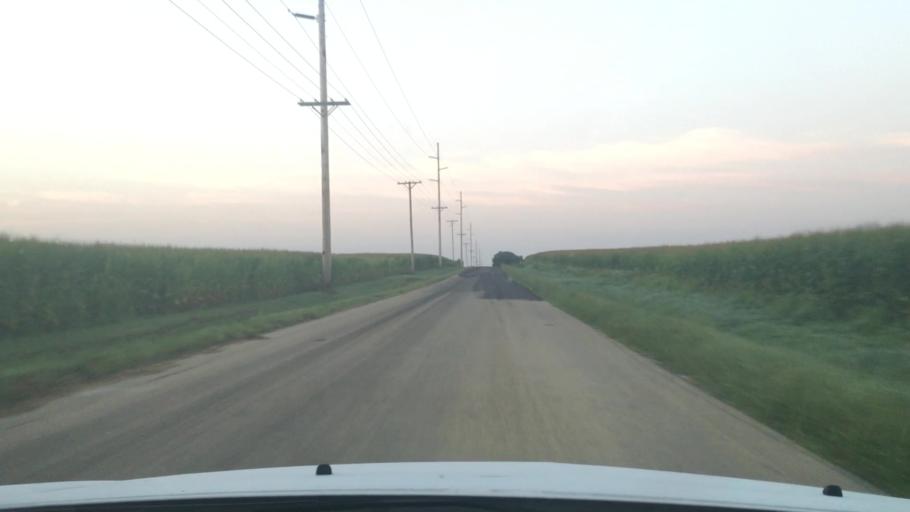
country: US
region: Illinois
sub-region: Ogle County
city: Rochelle
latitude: 41.9190
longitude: -89.0001
